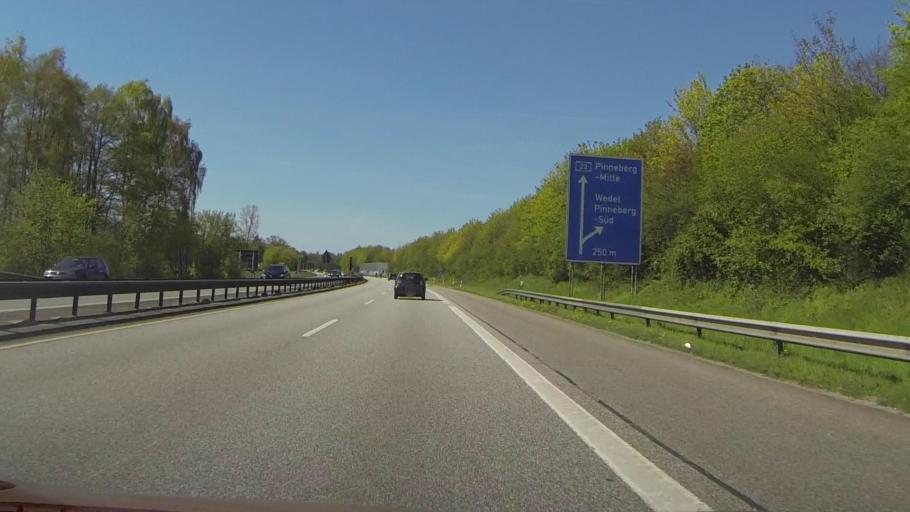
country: DE
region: Schleswig-Holstein
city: Rellingen
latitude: 53.6444
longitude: 9.8317
